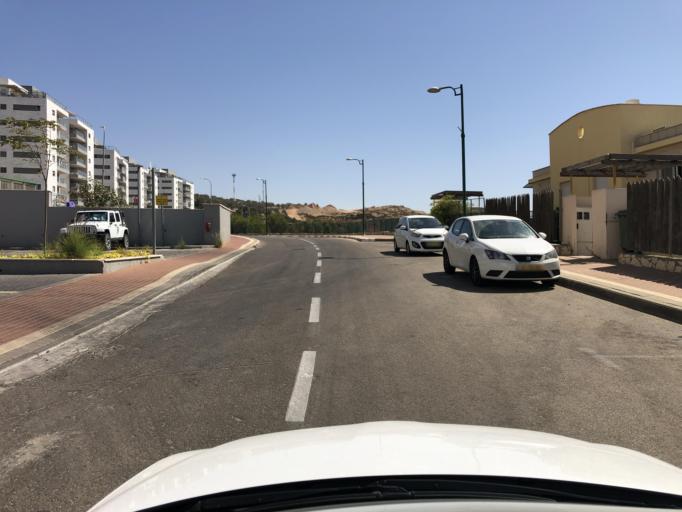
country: PS
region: West Bank
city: An Nabi Ilyas
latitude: 32.1654
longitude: 35.0187
